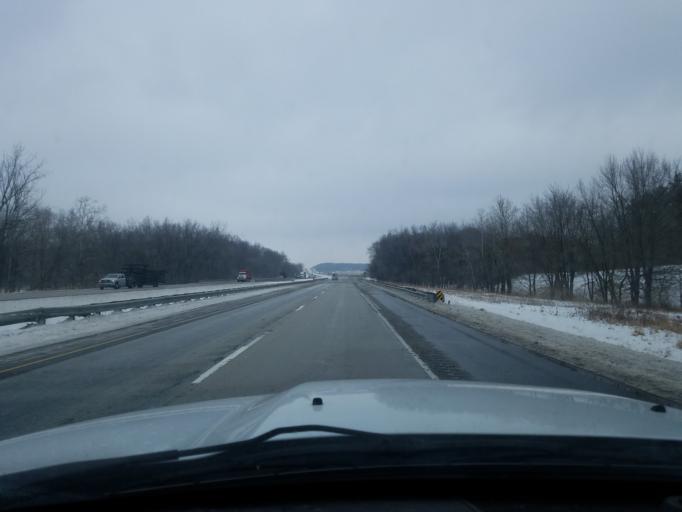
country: US
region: Indiana
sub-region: Fulton County
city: Rochester
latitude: 41.0935
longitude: -86.2403
